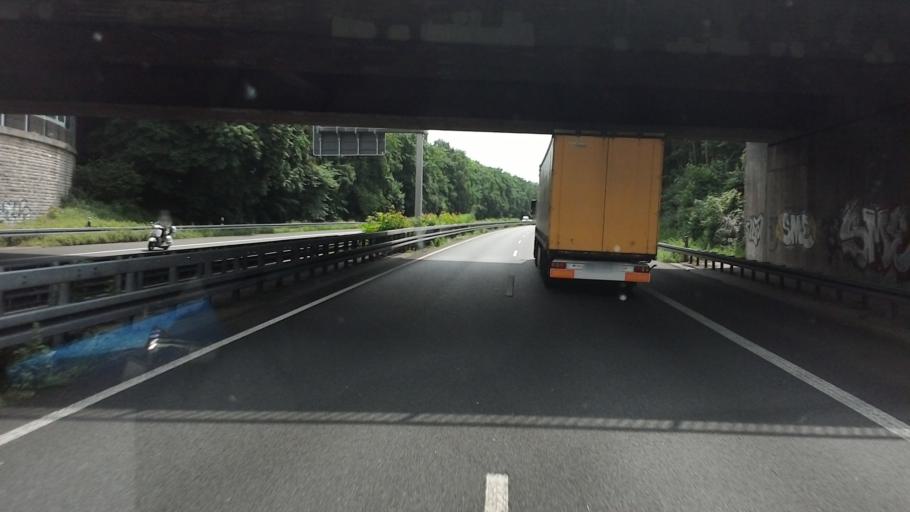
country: DE
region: North Rhine-Westphalia
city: Stolberg
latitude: 50.7782
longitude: 6.1775
